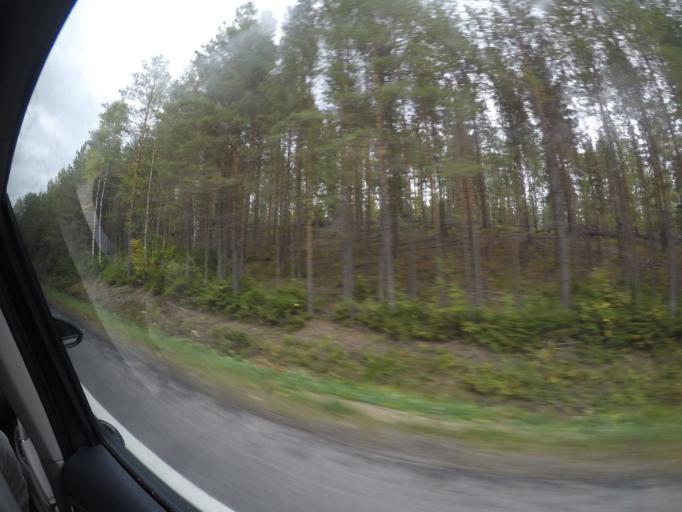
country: FI
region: Haeme
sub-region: Haemeenlinna
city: Parola
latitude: 61.1656
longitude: 24.4110
